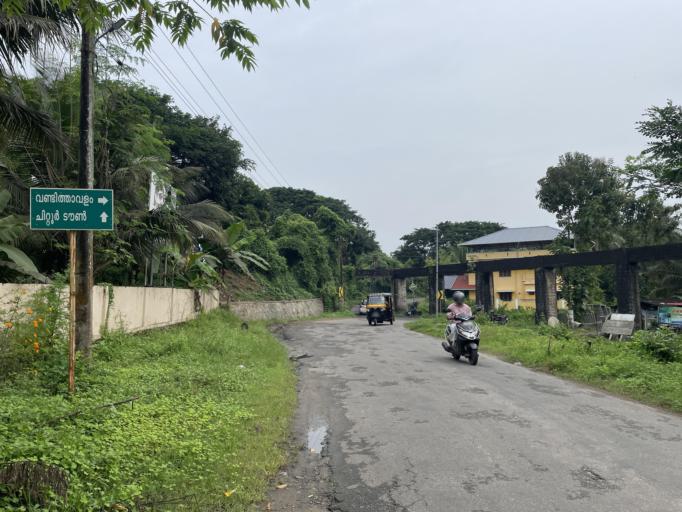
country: IN
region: Kerala
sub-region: Palakkad district
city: Chittur
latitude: 10.6931
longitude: 76.7431
